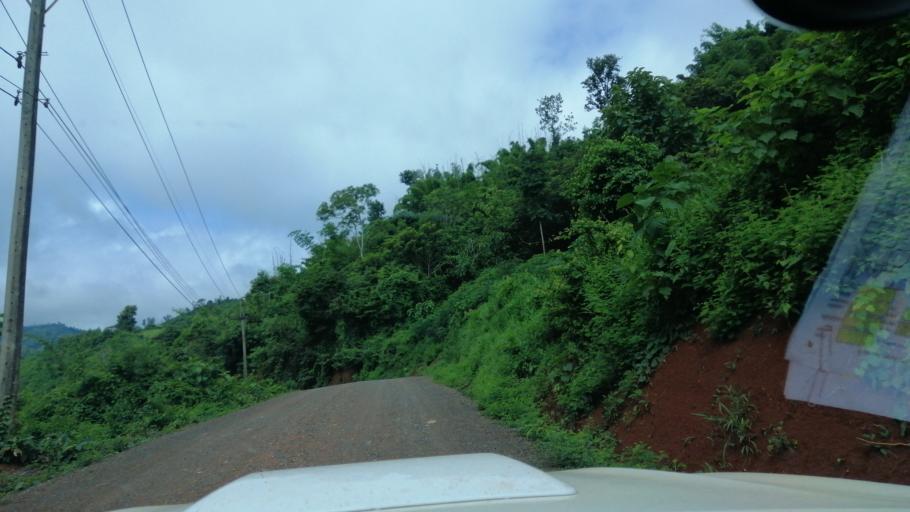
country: LA
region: Xiagnabouli
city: Muang Kenthao
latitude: 17.9173
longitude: 101.3641
